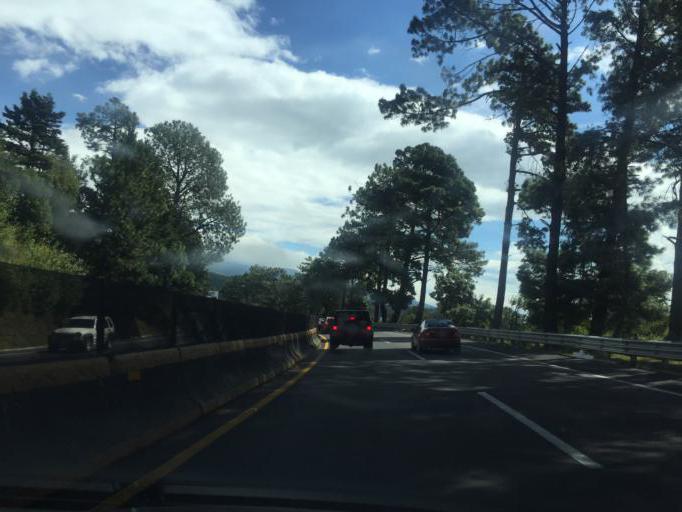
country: MX
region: Morelos
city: Tres Marias
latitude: 19.0309
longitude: -99.2132
